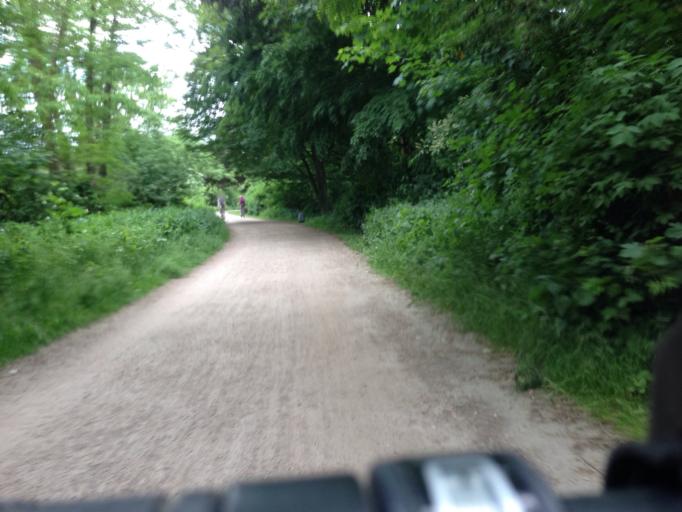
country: DE
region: Hamburg
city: Marienthal
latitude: 53.5782
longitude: 10.0803
